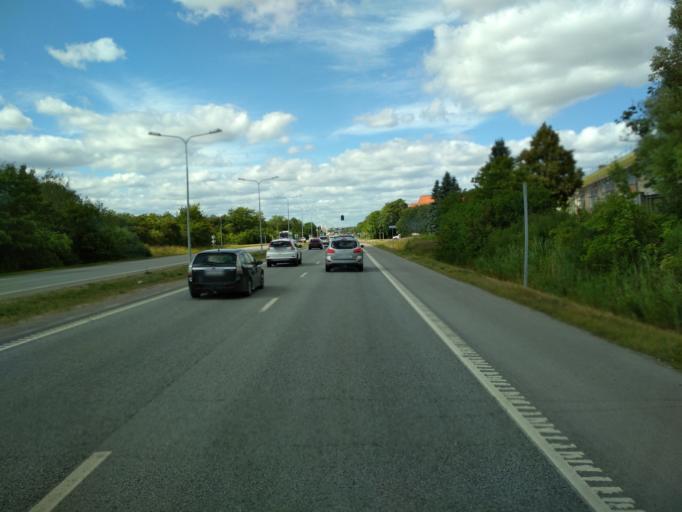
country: SE
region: Uppsala
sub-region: Uppsala Kommun
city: Uppsala
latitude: 59.8628
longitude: 17.6702
